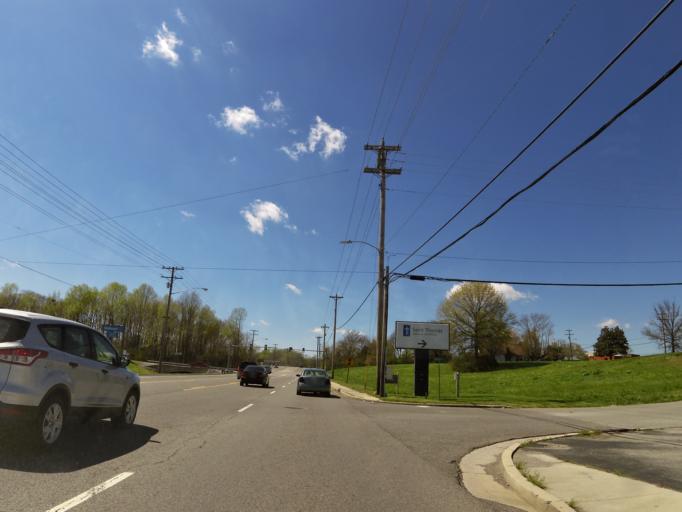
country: US
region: Tennessee
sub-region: DeKalb County
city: Smithville
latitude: 35.9586
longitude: -85.8279
